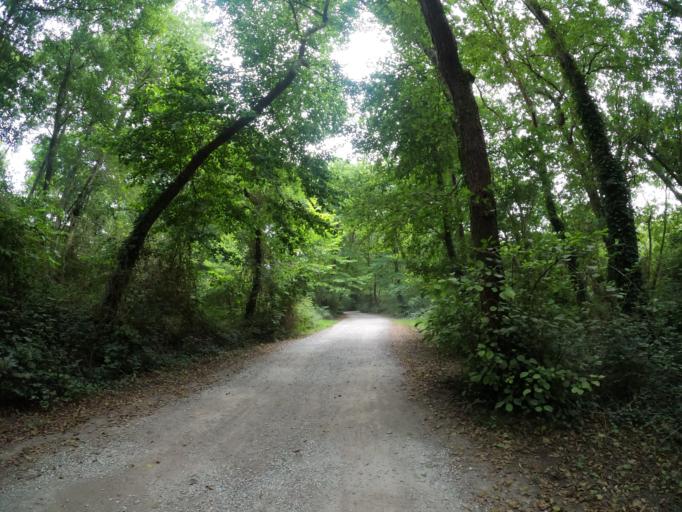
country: FR
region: Aquitaine
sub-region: Departement des Landes
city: Leon
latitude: 43.8867
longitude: -1.3086
